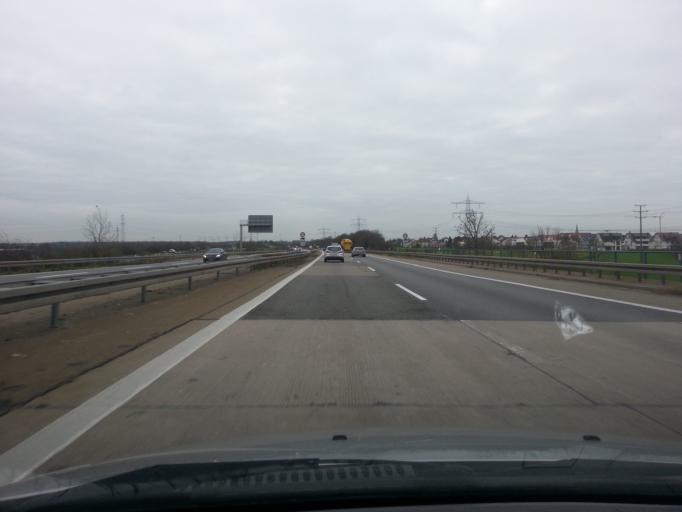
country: DE
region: Baden-Wuerttemberg
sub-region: Karlsruhe Region
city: Bruhl
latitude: 49.4038
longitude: 8.5456
